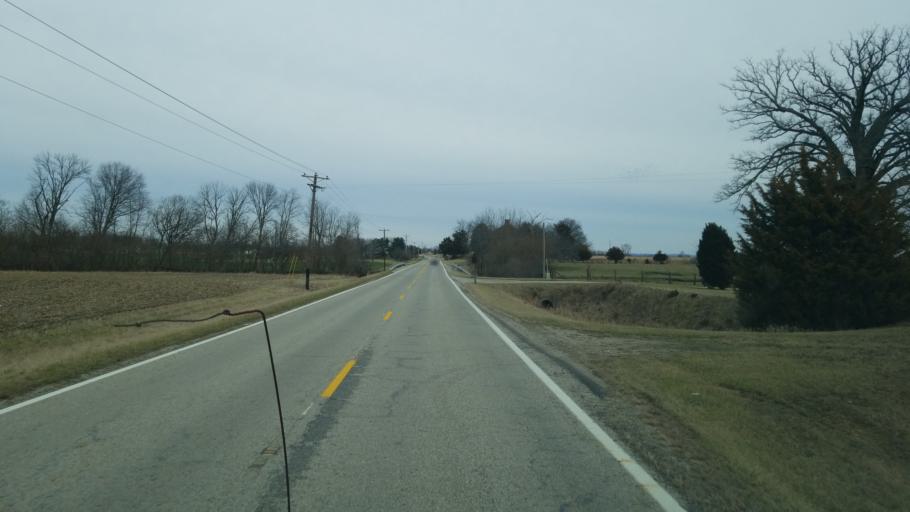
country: US
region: Ohio
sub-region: Pickaway County
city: Williamsport
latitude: 39.5665
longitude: -83.0713
